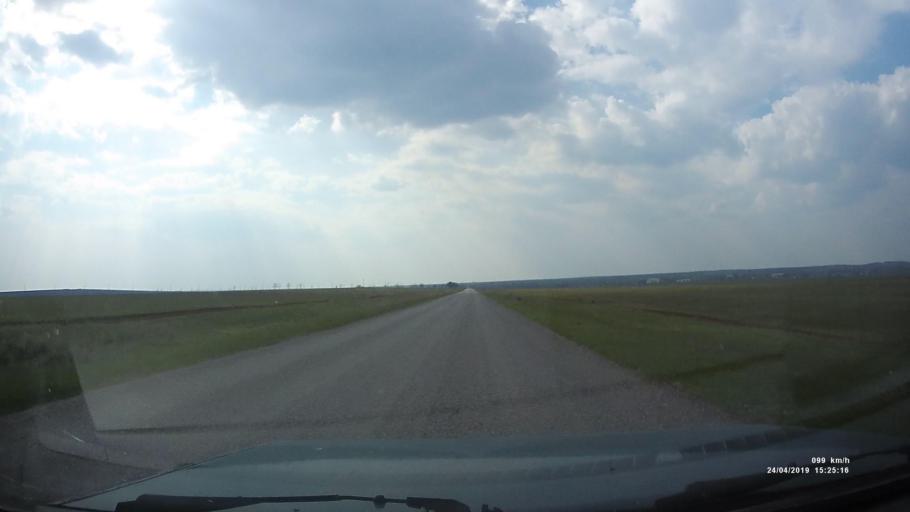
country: RU
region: Rostov
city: Remontnoye
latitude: 46.5517
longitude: 43.0511
